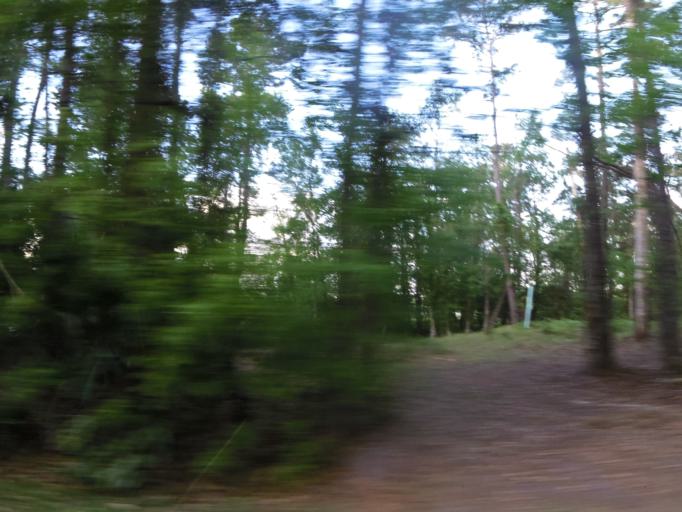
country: US
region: Florida
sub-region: Saint Johns County
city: Fruit Cove
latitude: 30.1276
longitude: -81.6085
